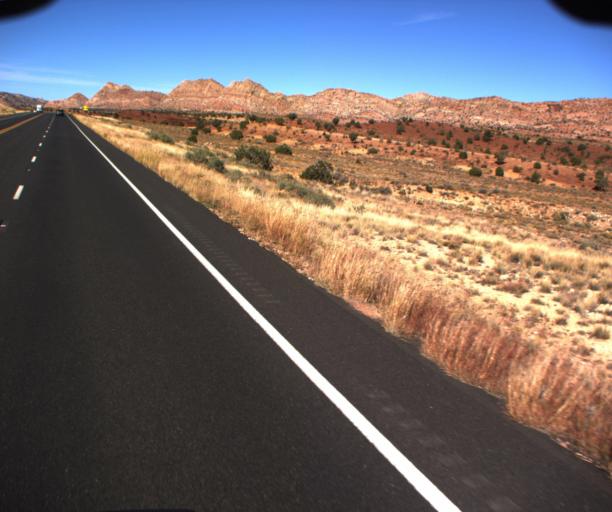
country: US
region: Arizona
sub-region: Coconino County
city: Tuba City
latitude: 36.3529
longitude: -111.5059
